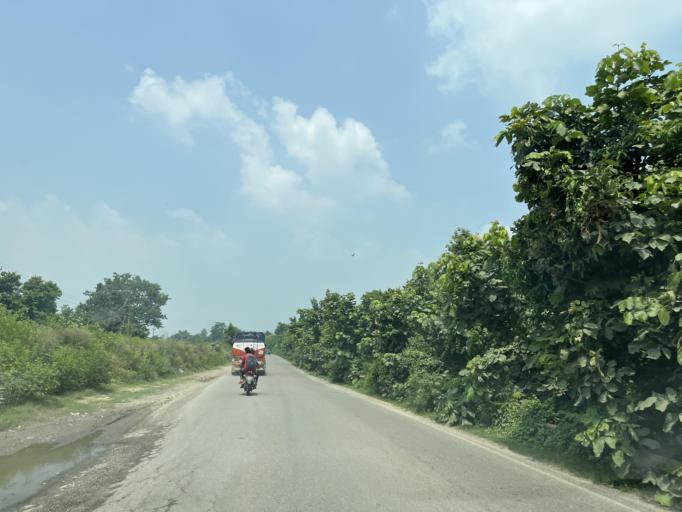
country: IN
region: Uttarakhand
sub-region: Haridwar
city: Haridwar
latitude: 29.8540
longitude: 78.1865
